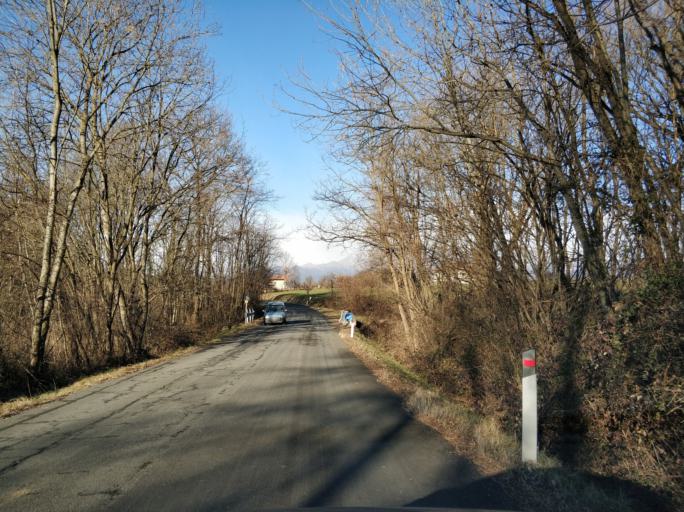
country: IT
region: Piedmont
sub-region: Provincia di Torino
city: Front
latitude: 45.2635
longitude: 7.6452
